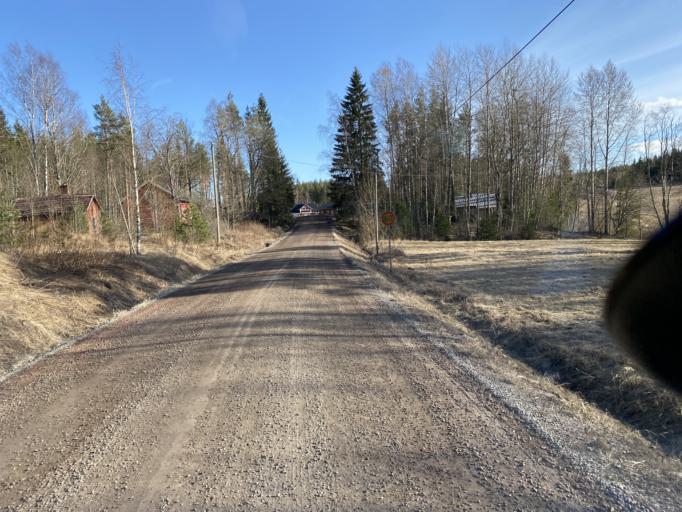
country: FI
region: Satakunta
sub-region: Rauma
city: Lappi
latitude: 61.1435
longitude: 21.9294
